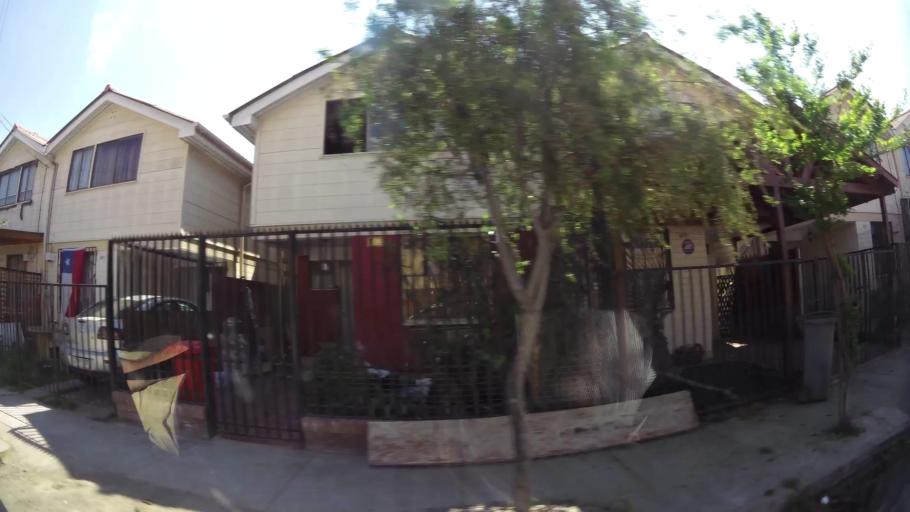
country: CL
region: Santiago Metropolitan
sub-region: Provincia de Talagante
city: Penaflor
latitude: -33.5730
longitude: -70.8053
